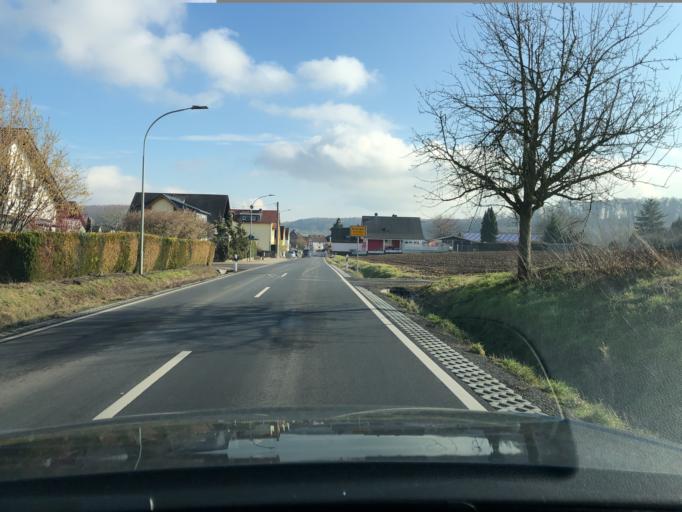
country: DE
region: Hesse
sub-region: Regierungsbezirk Darmstadt
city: Hammersbach
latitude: 50.2563
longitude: 9.0190
